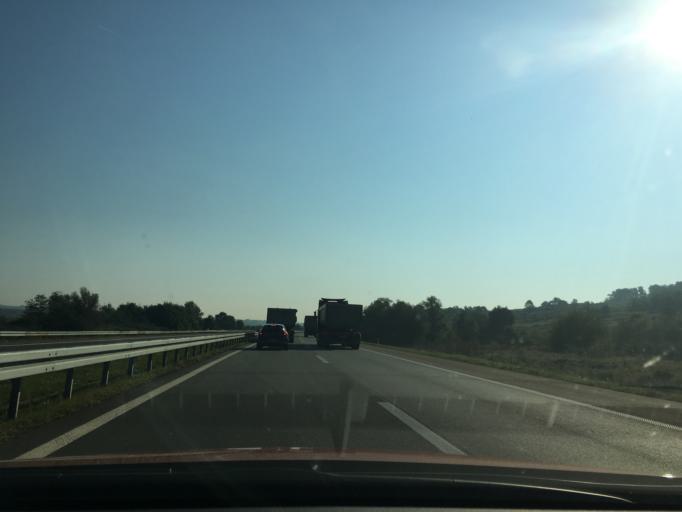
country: RS
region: Central Serbia
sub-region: Podunavski Okrug
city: Smederevo
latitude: 44.5865
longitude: 20.8556
